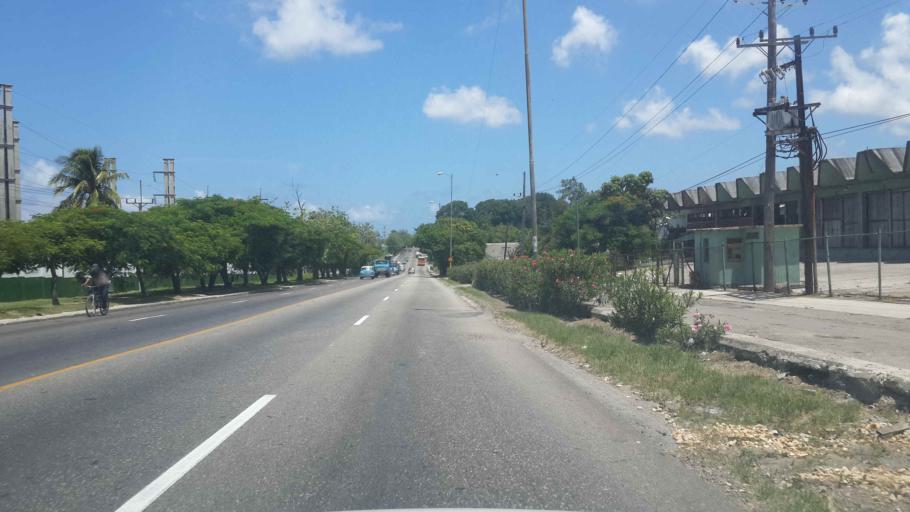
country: CU
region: La Habana
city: Guanabacoa
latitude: 23.1296
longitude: -82.3148
